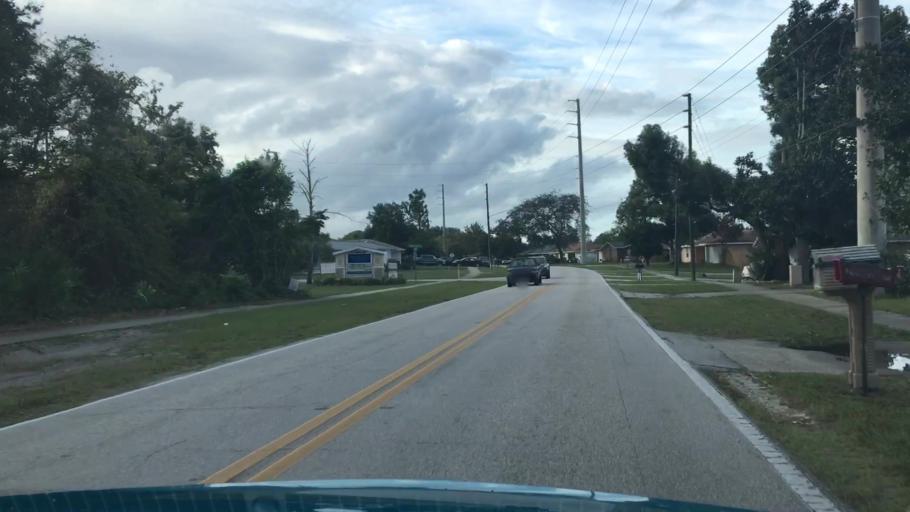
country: US
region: Florida
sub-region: Volusia County
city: Deltona
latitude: 28.8980
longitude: -81.2355
